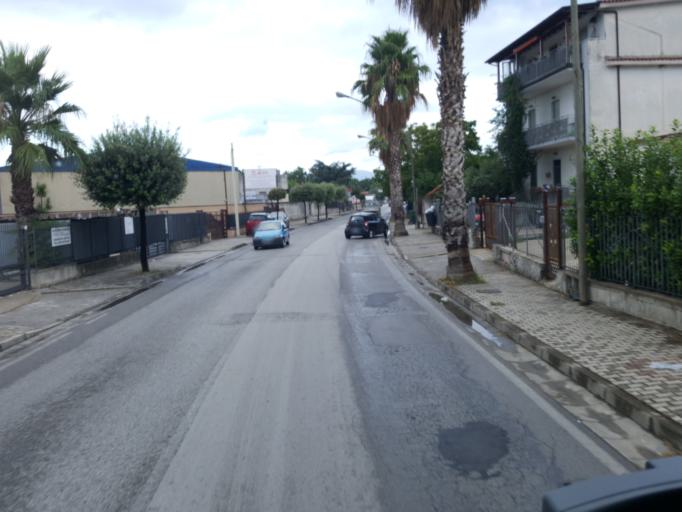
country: IT
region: Campania
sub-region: Provincia di Napoli
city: Palma Campania
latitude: 40.8610
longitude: 14.5487
